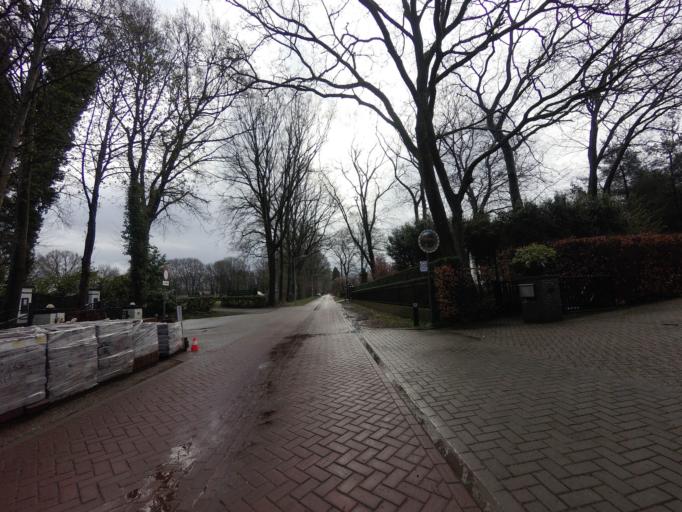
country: NL
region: Gelderland
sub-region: Gemeente Barneveld
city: Garderen
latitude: 52.2372
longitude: 5.7033
